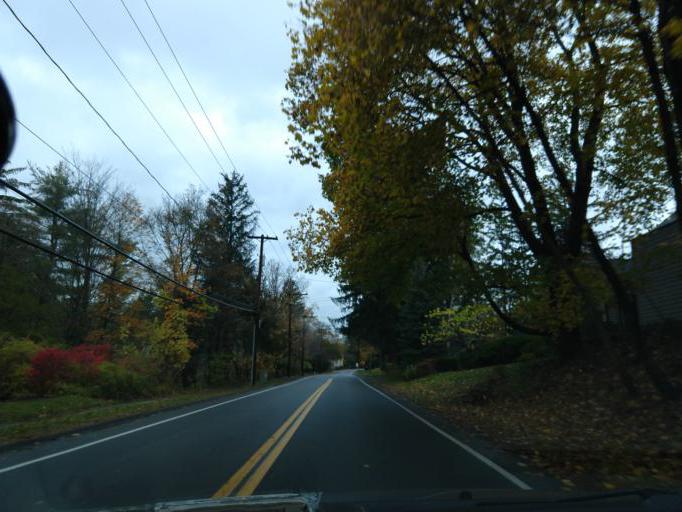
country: US
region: New York
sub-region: Tompkins County
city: Cayuga Heights
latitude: 42.4634
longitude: -76.4836
